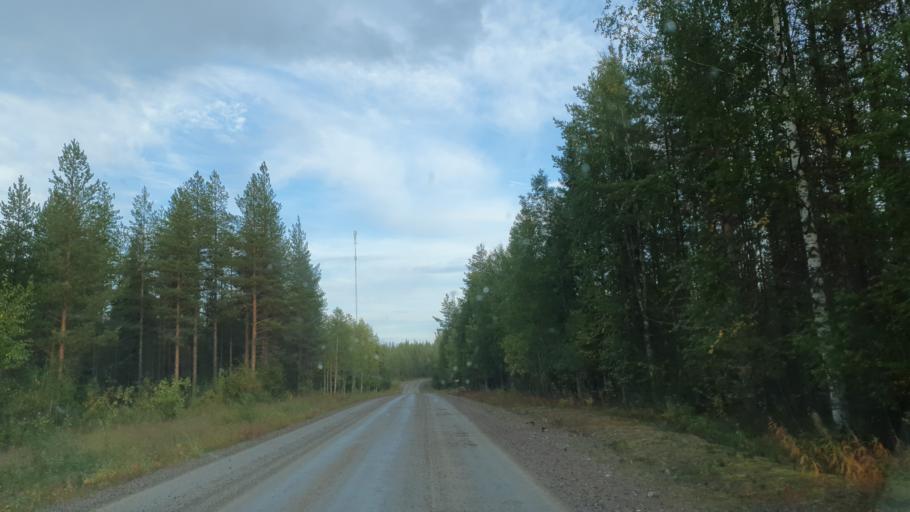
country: FI
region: Kainuu
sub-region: Kehys-Kainuu
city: Kuhmo
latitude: 64.4154
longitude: 29.5140
